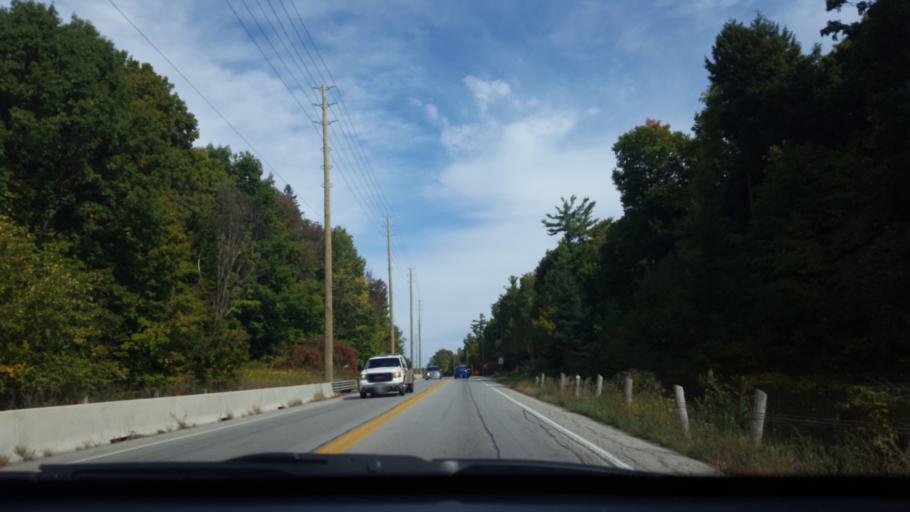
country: CA
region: Ontario
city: Vaughan
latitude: 43.8376
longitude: -79.5940
